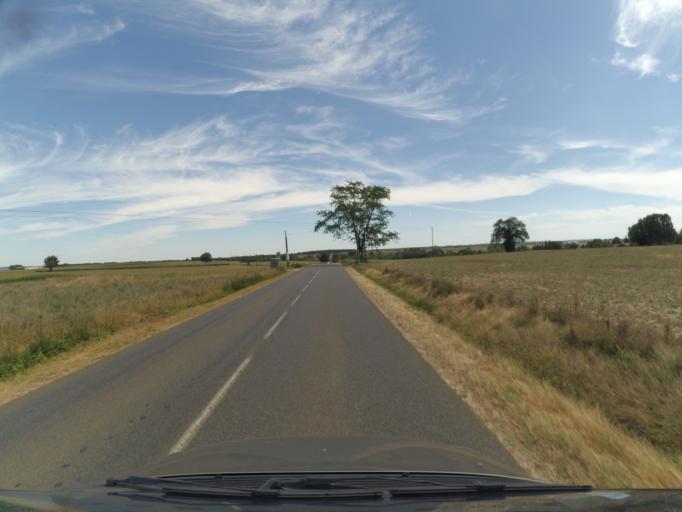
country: FR
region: Poitou-Charentes
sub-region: Departement de la Vienne
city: Celle-Levescault
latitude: 46.4176
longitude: 0.2150
